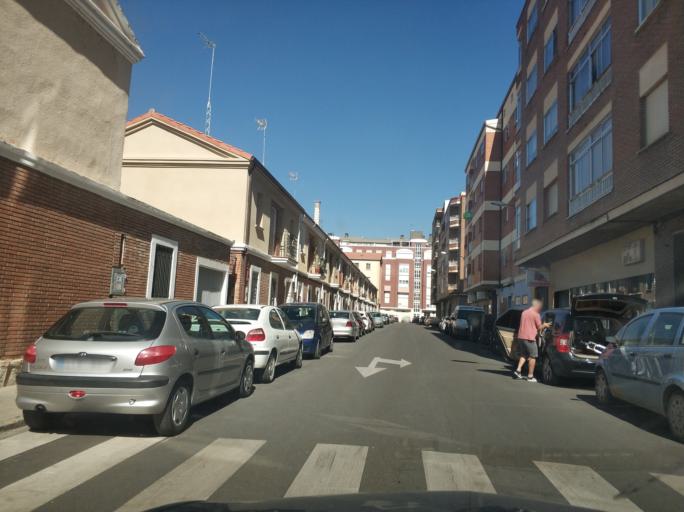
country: ES
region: Castille and Leon
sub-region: Provincia de Burgos
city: Aranda de Duero
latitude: 41.6715
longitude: -3.6772
